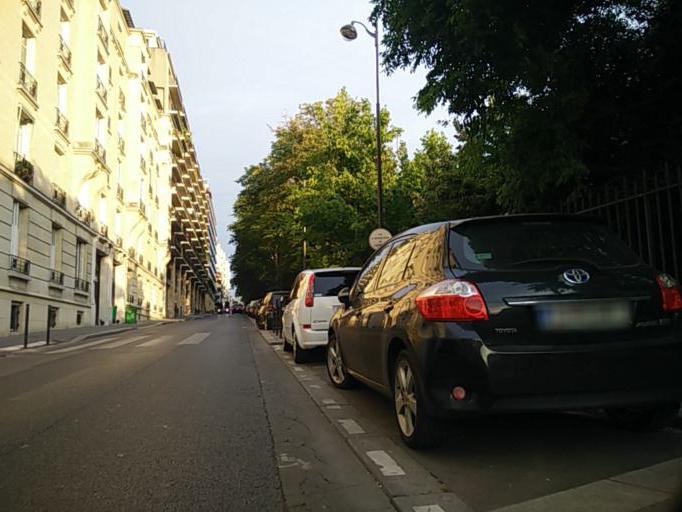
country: FR
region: Ile-de-France
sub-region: Departement de Seine-Saint-Denis
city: Le Pre-Saint-Gervais
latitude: 48.8824
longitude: 2.3862
